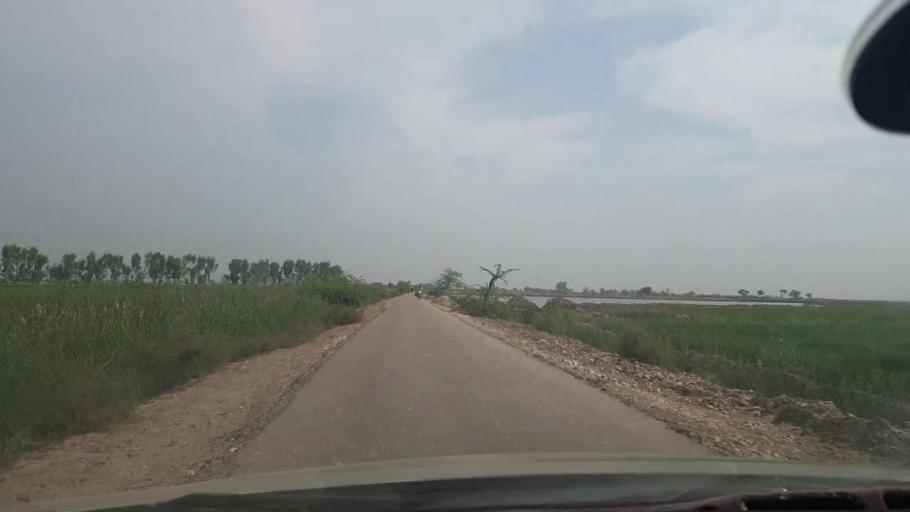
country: PK
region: Sindh
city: Jacobabad
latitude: 28.3074
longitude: 68.4757
